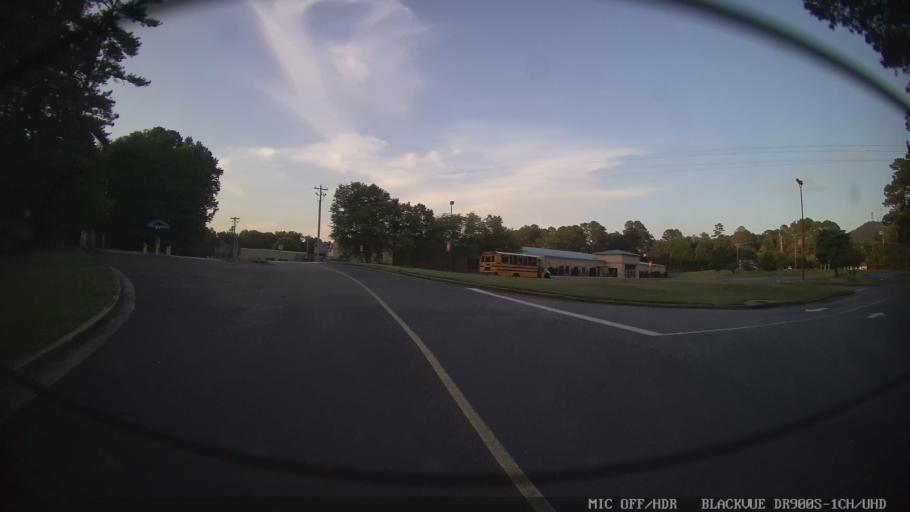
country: US
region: Georgia
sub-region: Forsyth County
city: Cumming
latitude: 34.2418
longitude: -84.1731
